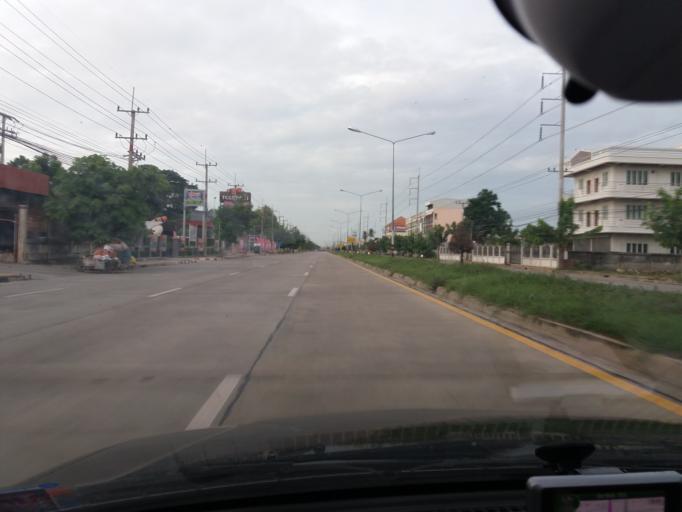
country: TH
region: Suphan Buri
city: U Thong
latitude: 14.3921
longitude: 99.8954
